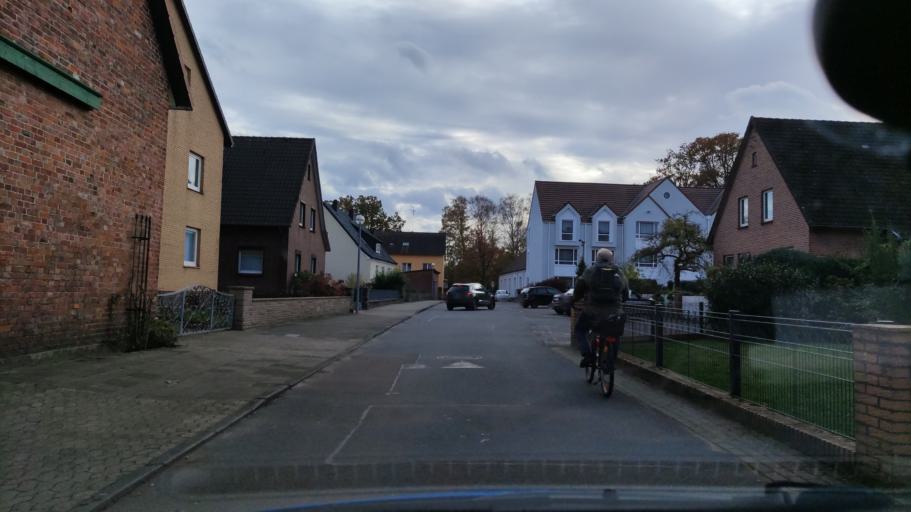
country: DE
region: Lower Saxony
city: Uelzen
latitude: 52.9577
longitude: 10.5471
